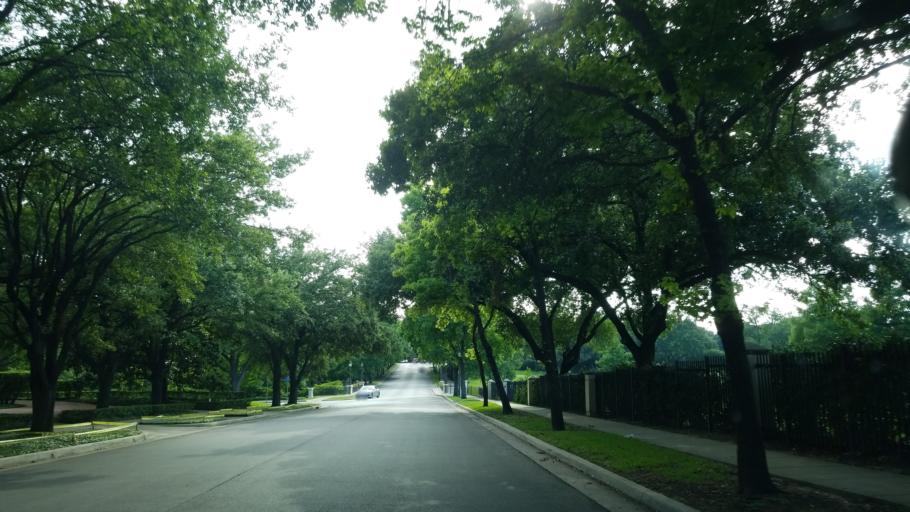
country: US
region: Texas
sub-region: Dallas County
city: Highland Park
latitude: 32.8324
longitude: -96.8013
